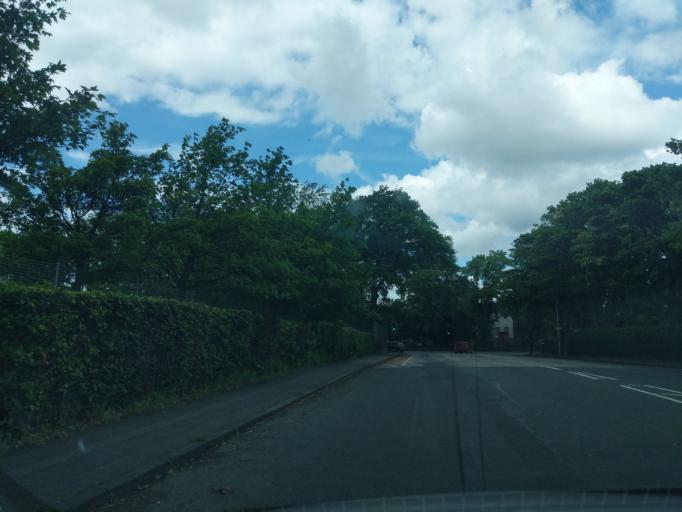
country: GB
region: Scotland
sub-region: Edinburgh
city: Edinburgh
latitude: 55.9689
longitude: -3.2254
